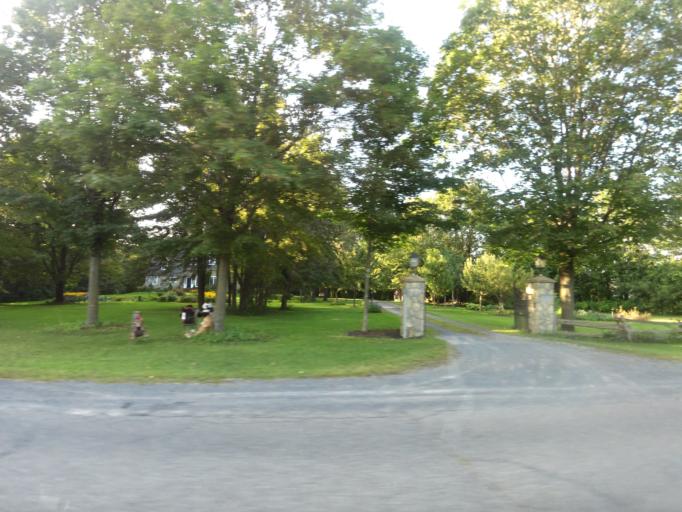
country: CA
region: Ontario
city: Clarence-Rockland
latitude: 45.4957
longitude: -75.4466
